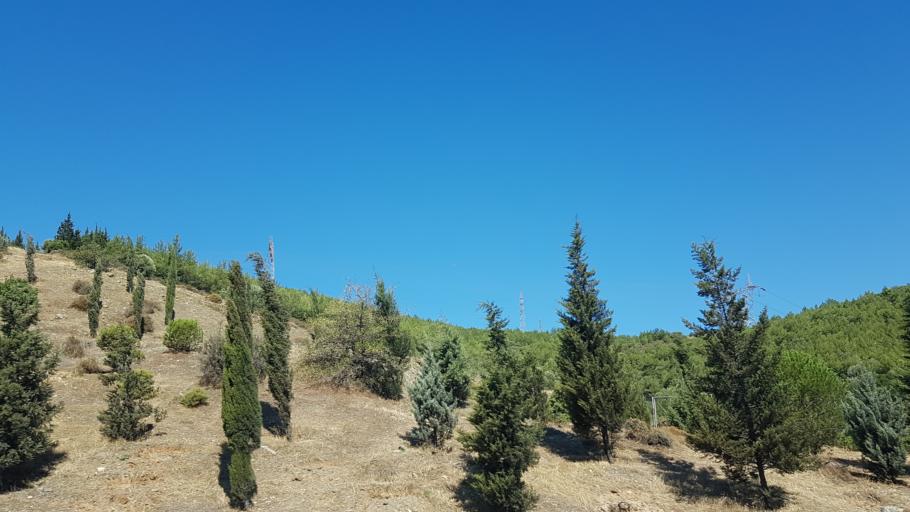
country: TR
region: Izmir
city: Buca
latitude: 38.4063
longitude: 27.2333
